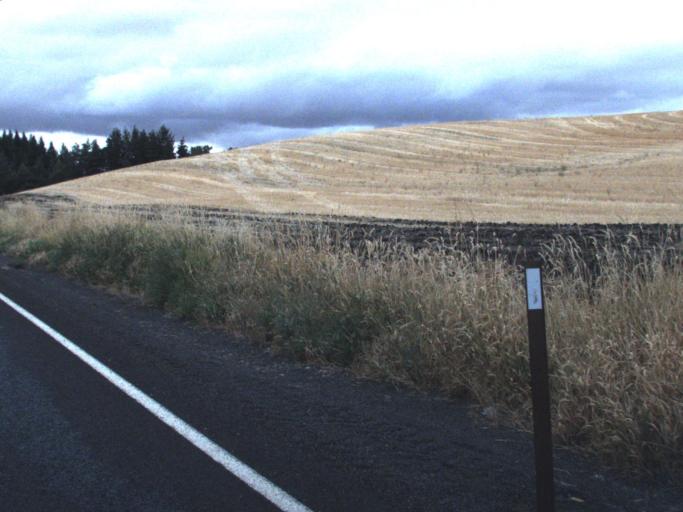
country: US
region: Washington
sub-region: Whitman County
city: Colfax
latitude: 47.1762
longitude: -117.2926
